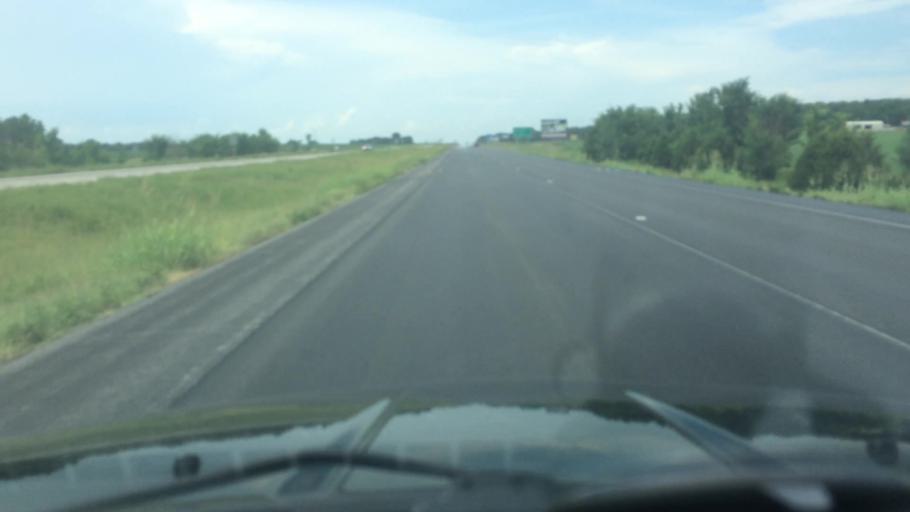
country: US
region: Missouri
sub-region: Saint Clair County
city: Osceola
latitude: 37.9866
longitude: -93.6509
